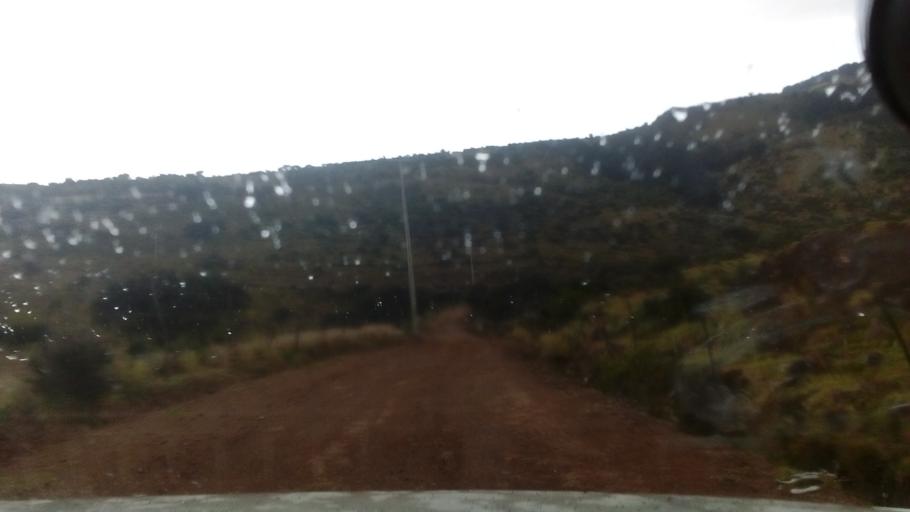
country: MX
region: Guanajuato
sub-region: Silao de la Victoria
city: San Francisco (Banos de Agua Caliente)
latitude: 21.1579
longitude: -101.4367
